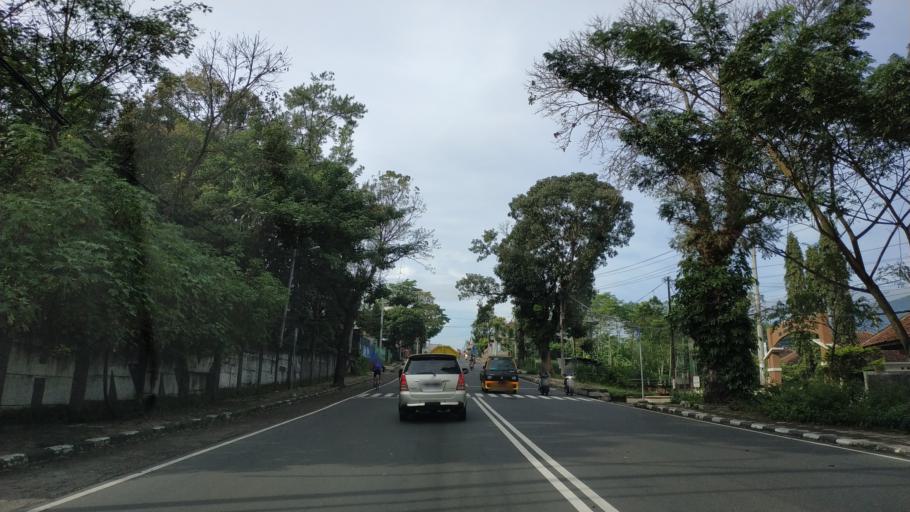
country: ID
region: Central Java
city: Salatiga
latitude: -7.3575
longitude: 110.5131
